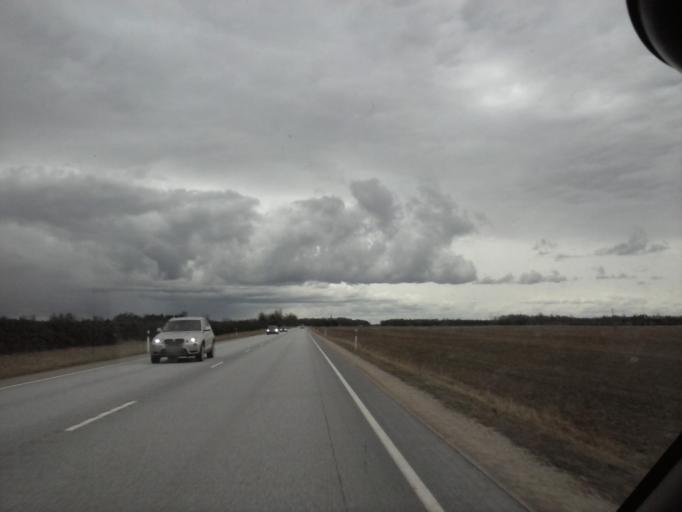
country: EE
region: Jaervamaa
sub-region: Paide linn
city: Paide
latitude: 58.7823
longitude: 25.7594
